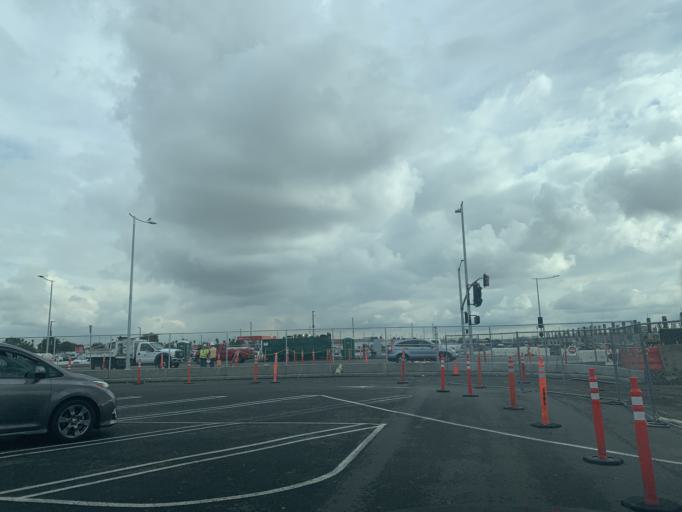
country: US
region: California
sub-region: Los Angeles County
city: El Segundo
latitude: 33.9515
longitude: -118.3925
